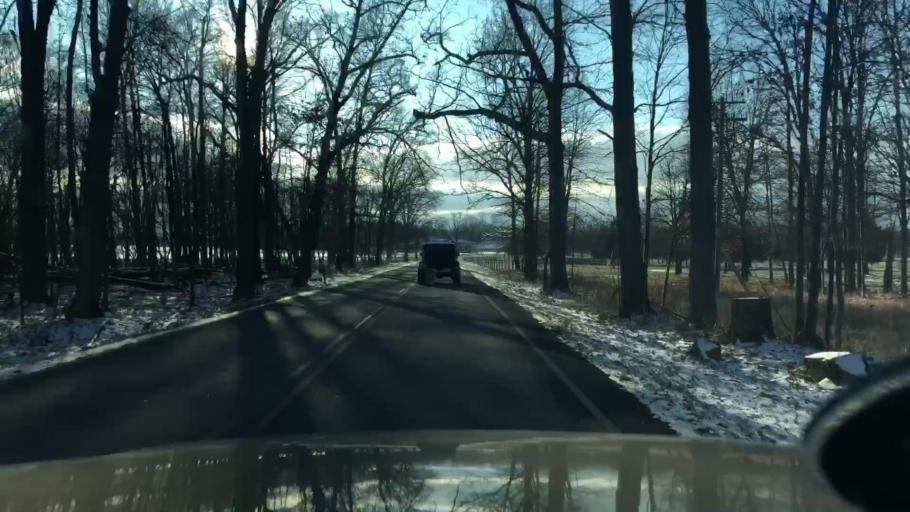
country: US
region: Michigan
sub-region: Jackson County
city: Vandercook Lake
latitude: 42.0954
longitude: -84.4602
